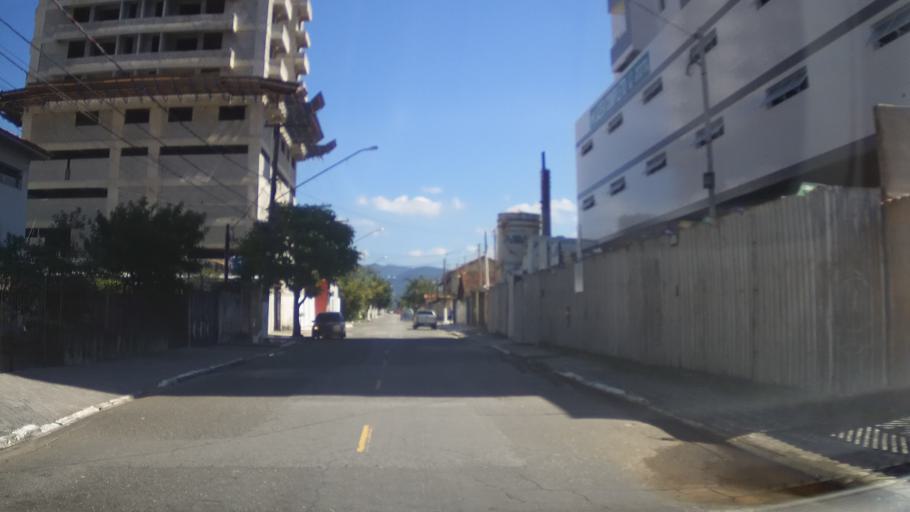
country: BR
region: Sao Paulo
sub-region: Praia Grande
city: Praia Grande
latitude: -24.0248
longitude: -46.4677
